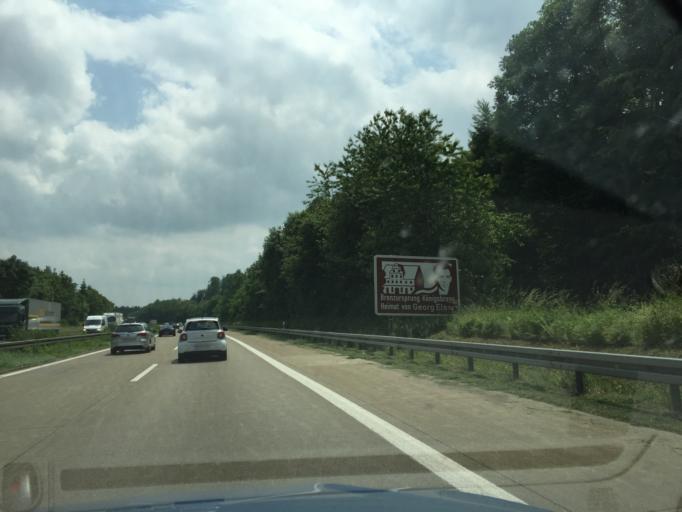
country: DE
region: Baden-Wuerttemberg
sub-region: Regierungsbezirk Stuttgart
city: Westhausen
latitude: 48.8461
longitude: 10.1973
